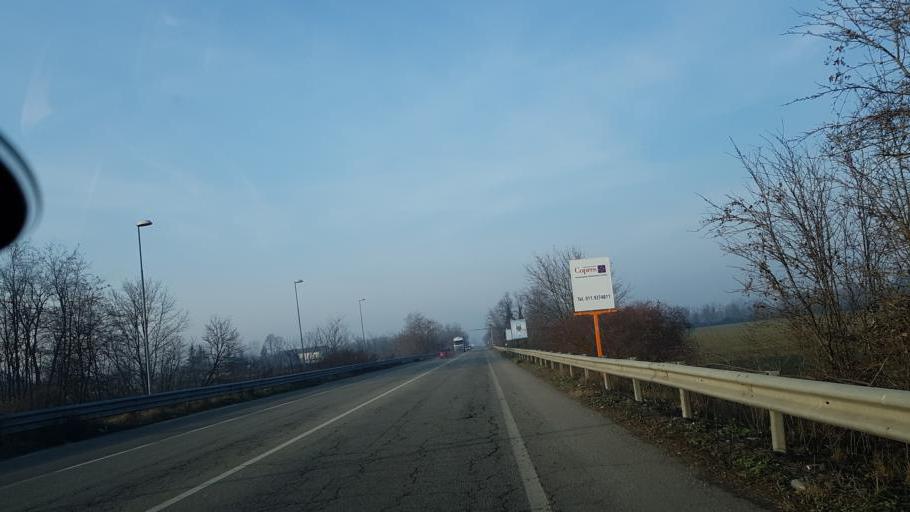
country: IT
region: Piedmont
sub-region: Provincia di Alessandria
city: Novi Ligure
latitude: 44.7742
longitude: 8.7996
